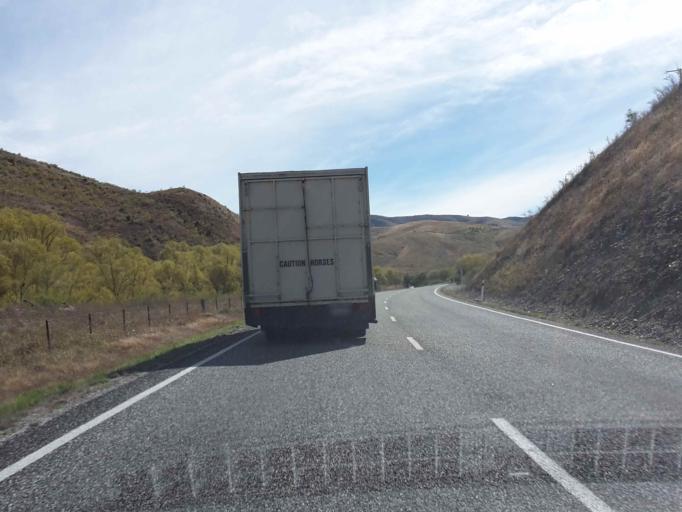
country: NZ
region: Otago
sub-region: Queenstown-Lakes District
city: Wanaka
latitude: -44.6835
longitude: 169.4834
